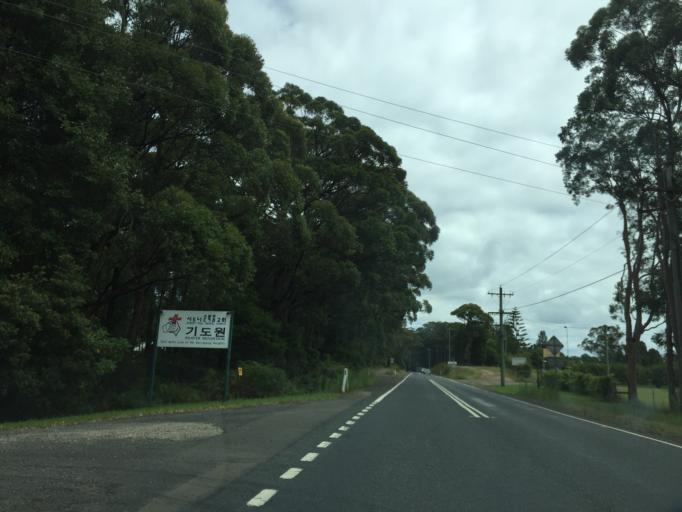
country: AU
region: New South Wales
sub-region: Hawkesbury
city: Richmond
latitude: -33.5184
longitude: 150.6147
